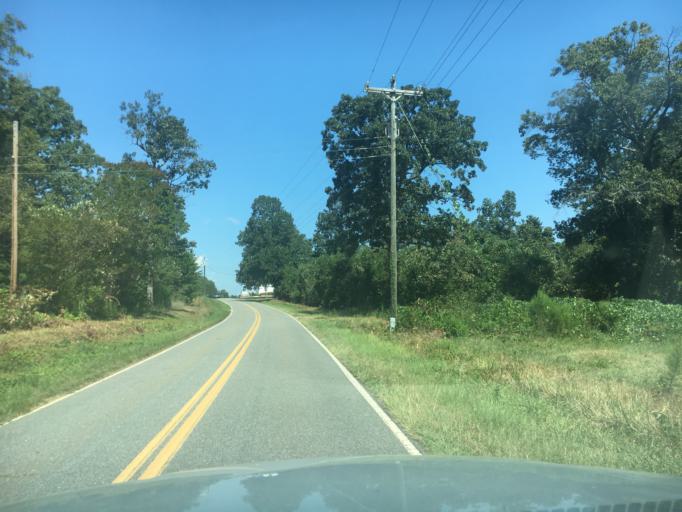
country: US
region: South Carolina
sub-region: Spartanburg County
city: Boiling Springs
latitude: 35.2022
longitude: -82.0210
